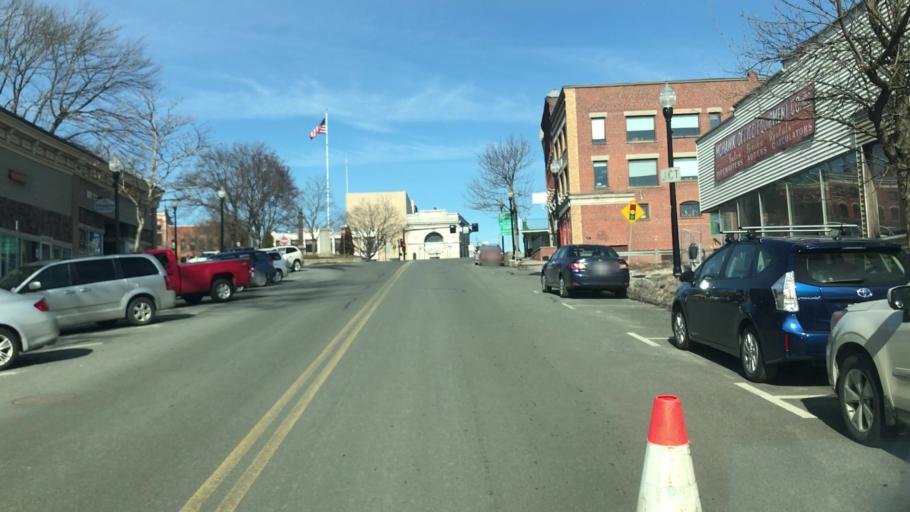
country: US
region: Massachusetts
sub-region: Franklin County
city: Greenfield
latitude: 42.5865
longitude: -72.6008
